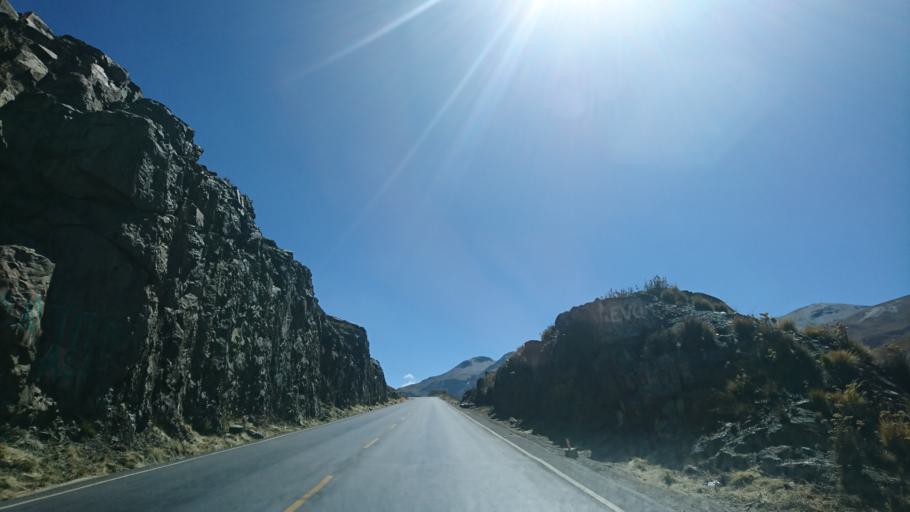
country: BO
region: La Paz
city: La Paz
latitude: -16.4079
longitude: -68.0501
